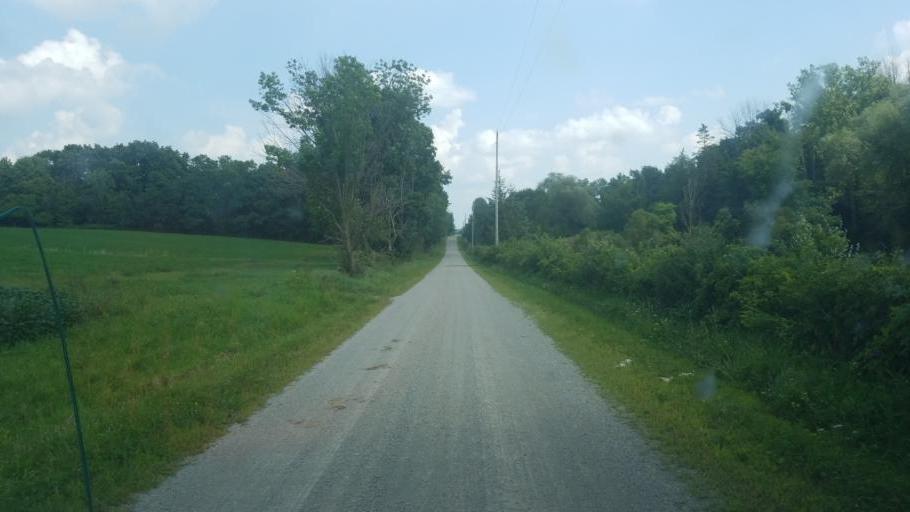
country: US
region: Ohio
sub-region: Huron County
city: New London
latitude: 41.0110
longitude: -82.4292
